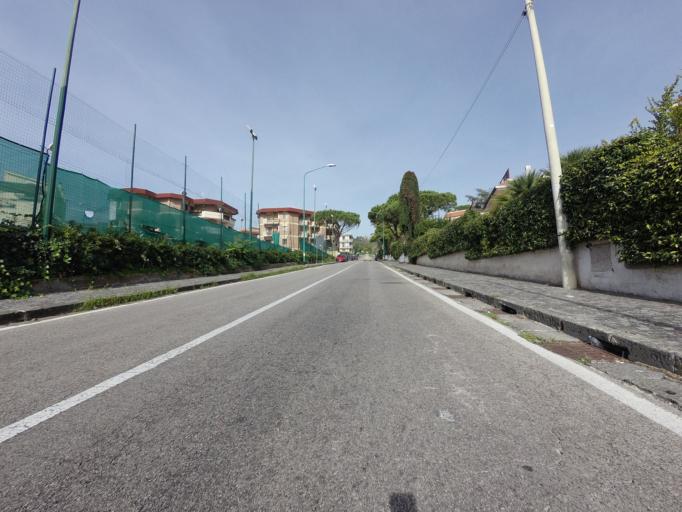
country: IT
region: Campania
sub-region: Provincia di Napoli
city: Ercolano
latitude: 40.8002
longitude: 14.3784
